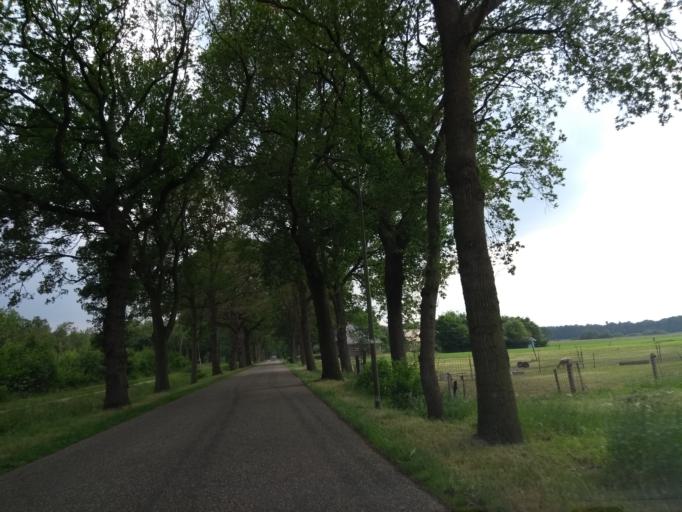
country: NL
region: Overijssel
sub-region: Gemeente Staphorst
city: Staphorst
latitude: 52.6454
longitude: 6.2871
